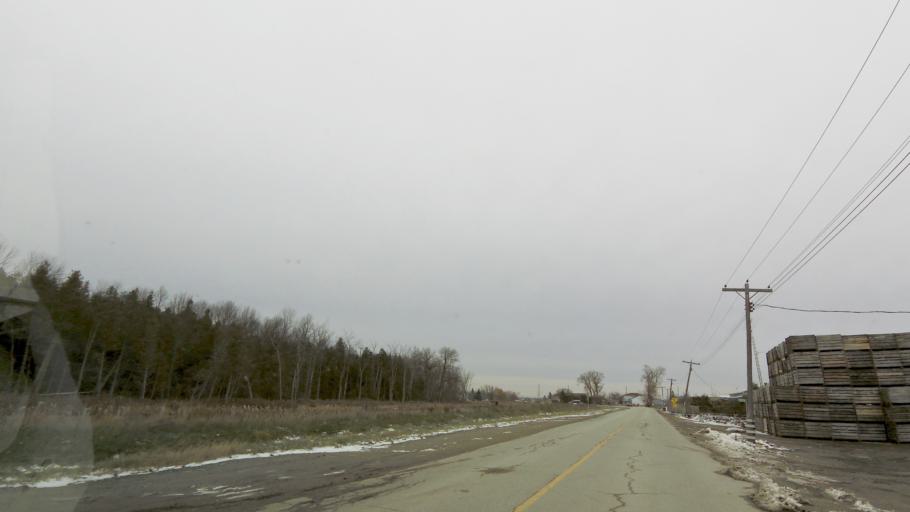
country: CA
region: Ontario
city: Bradford West Gwillimbury
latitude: 44.0867
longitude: -79.5713
